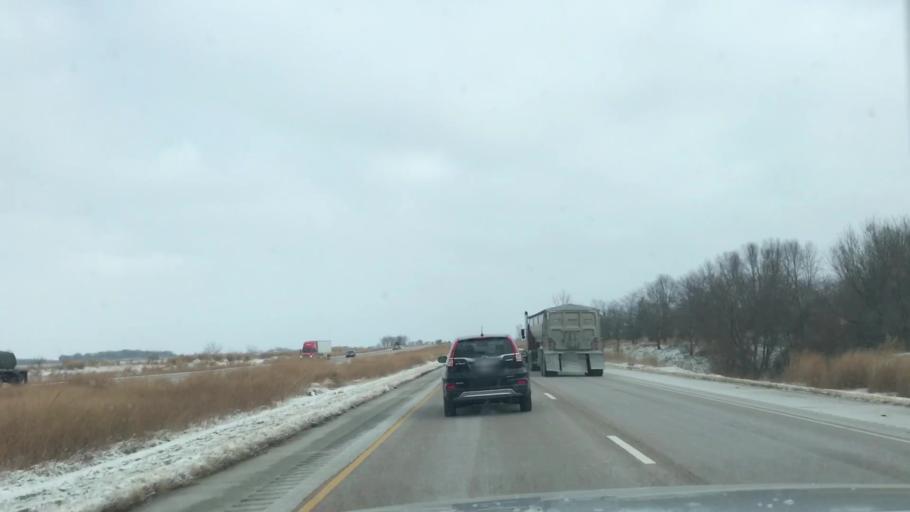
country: US
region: Illinois
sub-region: Macoupin County
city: Mount Olive
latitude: 39.1328
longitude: -89.7108
